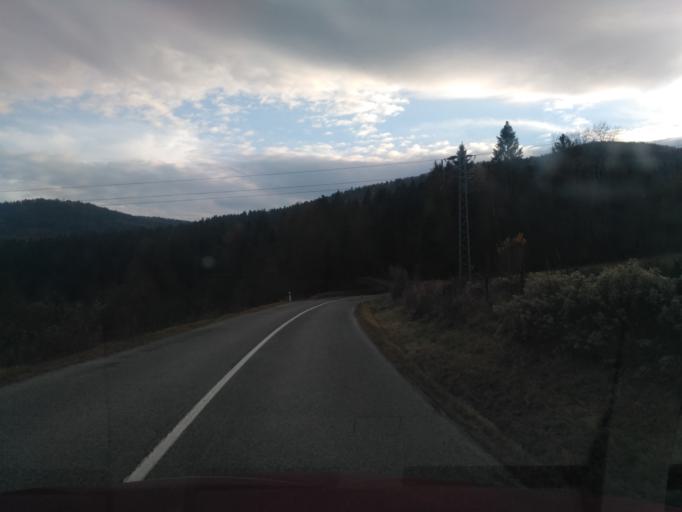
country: SK
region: Kosicky
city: Krompachy
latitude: 48.7966
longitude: 20.7493
